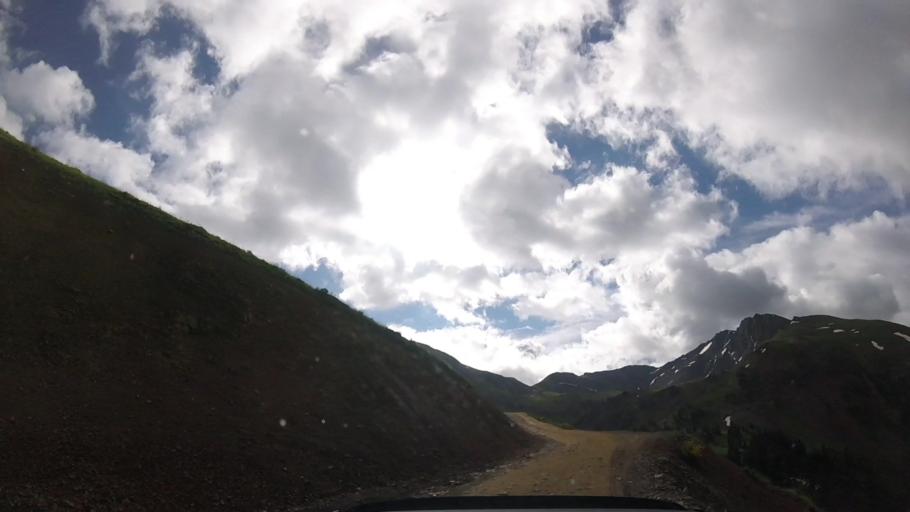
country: US
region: Colorado
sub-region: San Juan County
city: Silverton
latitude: 37.9133
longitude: -107.6409
